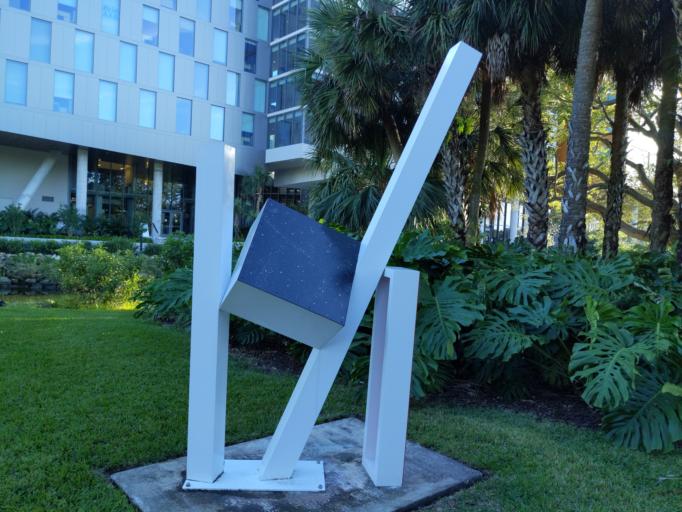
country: US
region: Florida
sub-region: Miami-Dade County
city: Coral Gables
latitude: 25.7192
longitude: -80.2773
